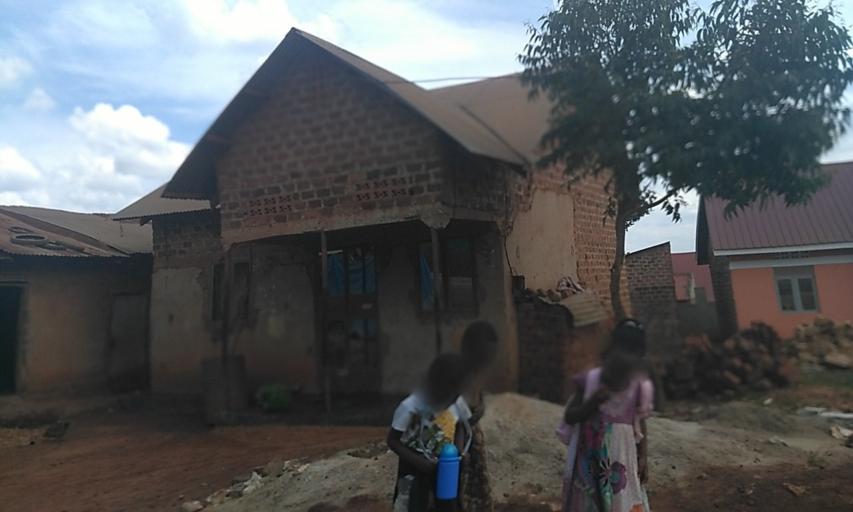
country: UG
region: Central Region
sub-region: Wakiso District
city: Wakiso
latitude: 0.3906
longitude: 32.4633
